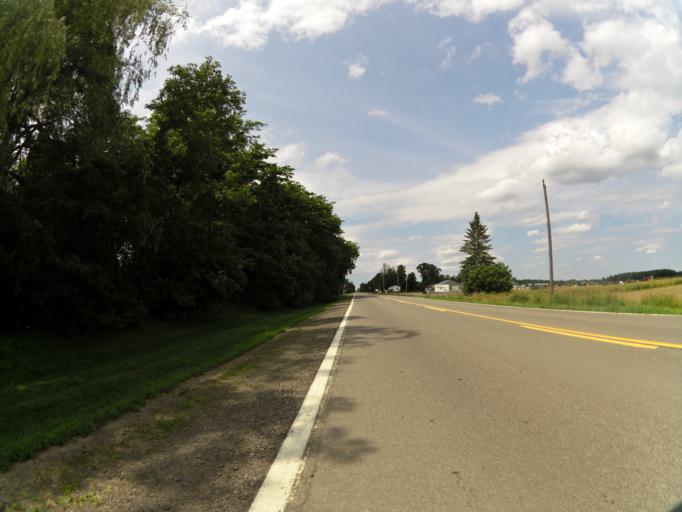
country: CA
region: Ontario
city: Ottawa
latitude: 45.1962
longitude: -75.5892
